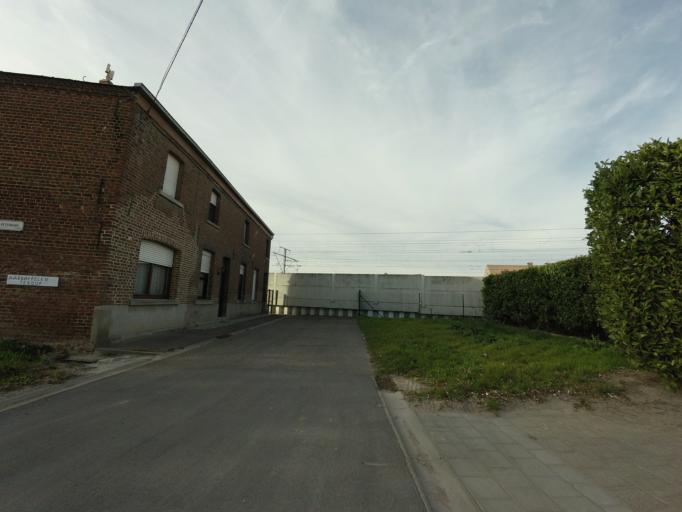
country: BE
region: Flanders
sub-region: Provincie Vlaams-Brabant
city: Bertem
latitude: 50.8984
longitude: 4.6121
